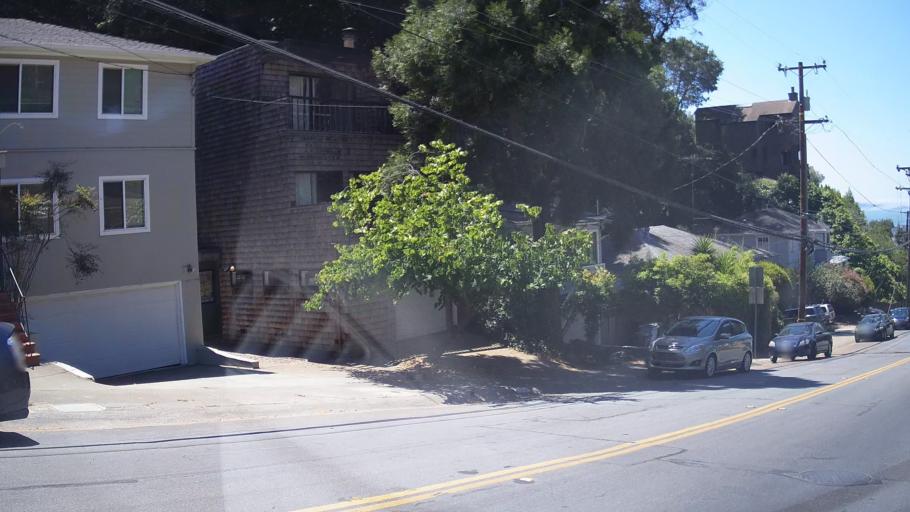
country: US
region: California
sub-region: Alameda County
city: Berkeley
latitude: 37.8846
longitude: -122.2550
